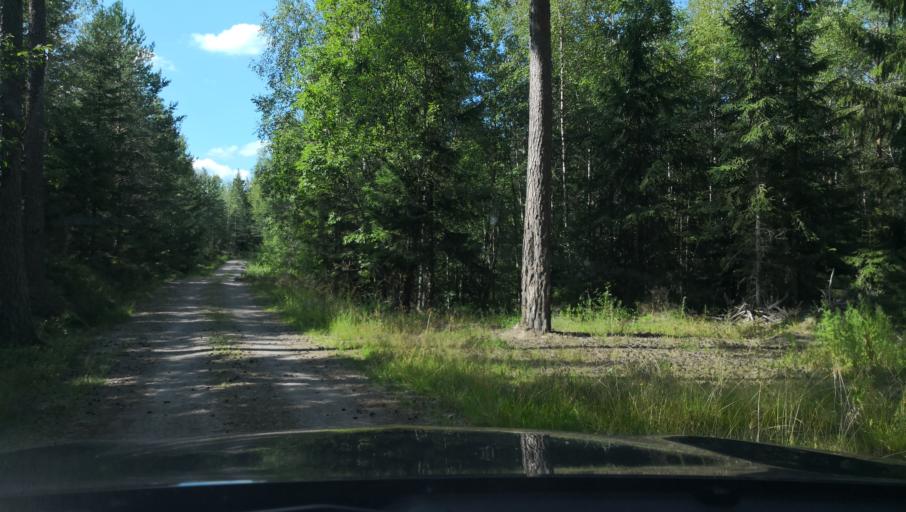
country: SE
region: Vaestmanland
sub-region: Vasteras
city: Skultuna
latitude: 59.7105
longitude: 16.3717
